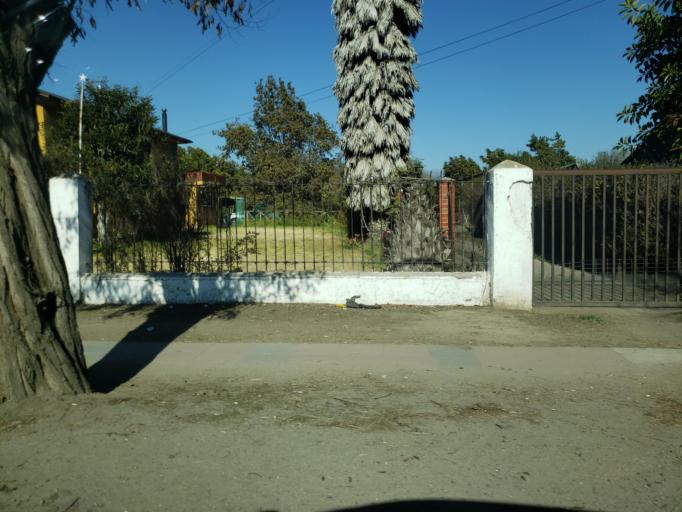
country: CL
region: Santiago Metropolitan
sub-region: Provincia de Talagante
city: El Monte
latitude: -33.6842
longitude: -71.0032
